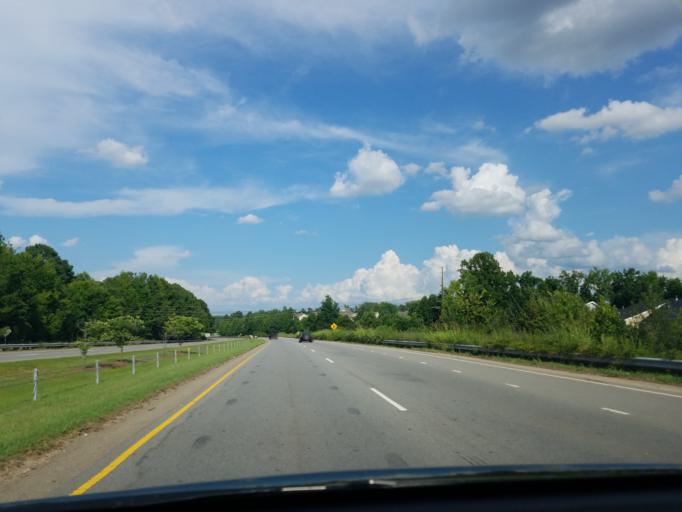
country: US
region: North Carolina
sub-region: Wake County
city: Apex
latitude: 35.7490
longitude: -78.8468
